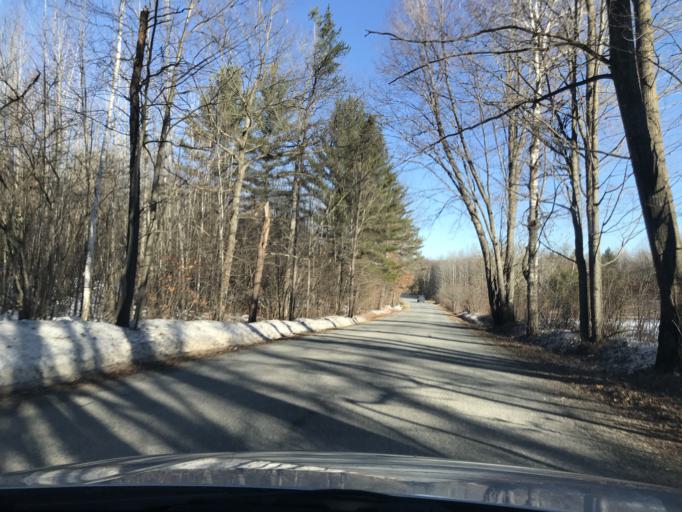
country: US
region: Wisconsin
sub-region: Marinette County
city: Niagara
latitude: 45.3829
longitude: -88.0400
